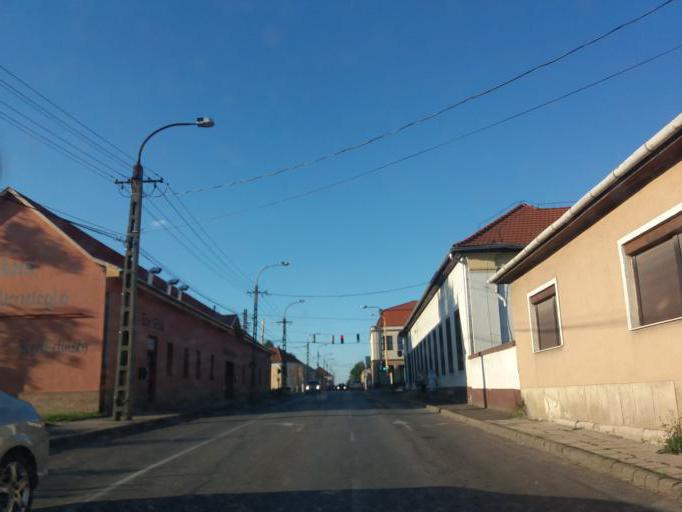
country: HU
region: Fejer
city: Martonvasar
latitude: 47.3133
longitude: 18.7881
